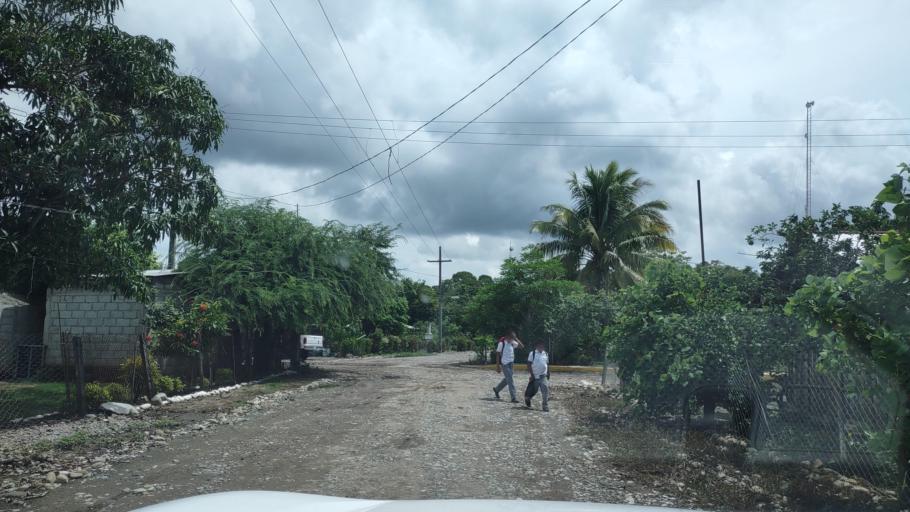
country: MX
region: Veracruz
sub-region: Alamo Temapache
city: Vegas de la Soledad y Soledad Dos
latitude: 20.9308
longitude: -97.7817
